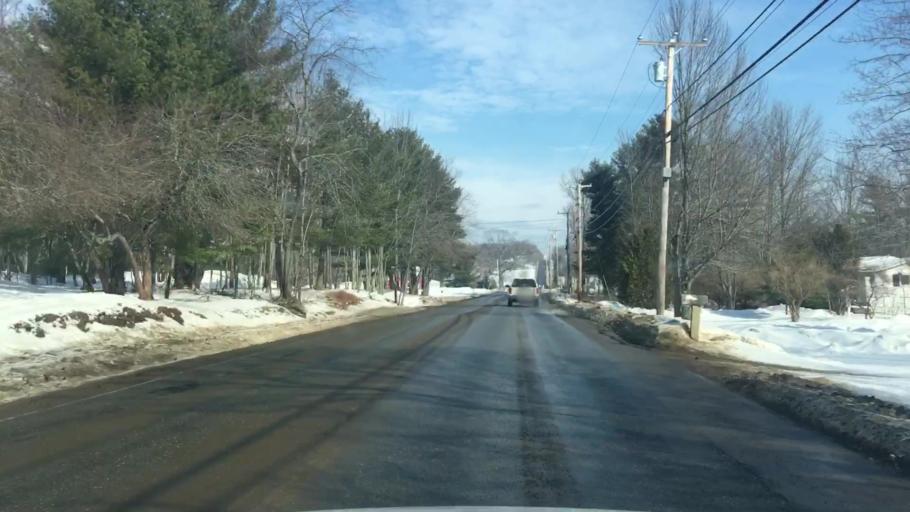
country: US
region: Maine
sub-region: Penobscot County
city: Hermon
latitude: 44.8273
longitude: -68.8874
